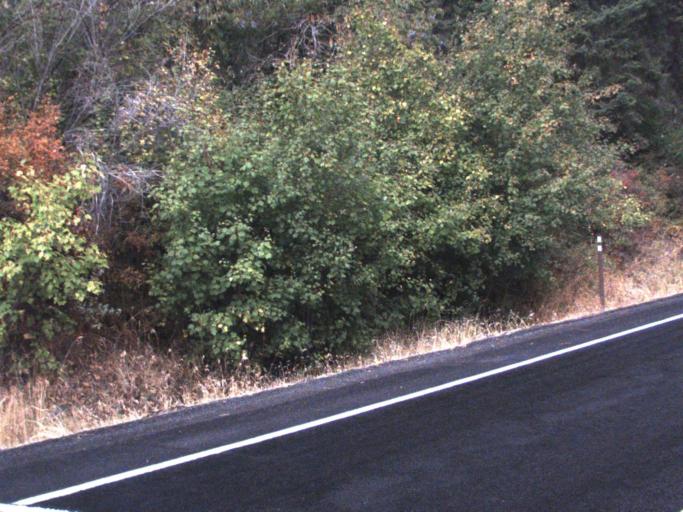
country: US
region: Washington
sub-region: Spokane County
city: Medical Lake
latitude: 47.7554
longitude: -117.8901
